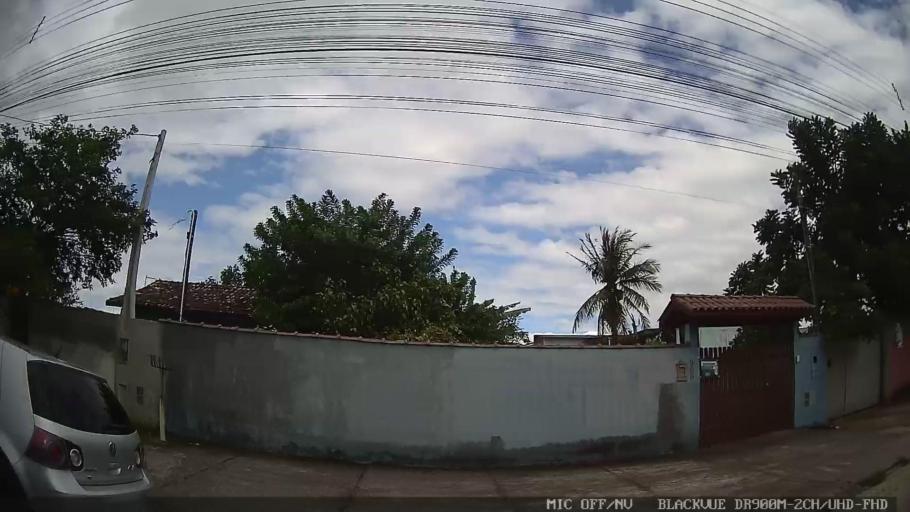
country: BR
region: Sao Paulo
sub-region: Caraguatatuba
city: Caraguatatuba
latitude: -23.6416
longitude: -45.4409
